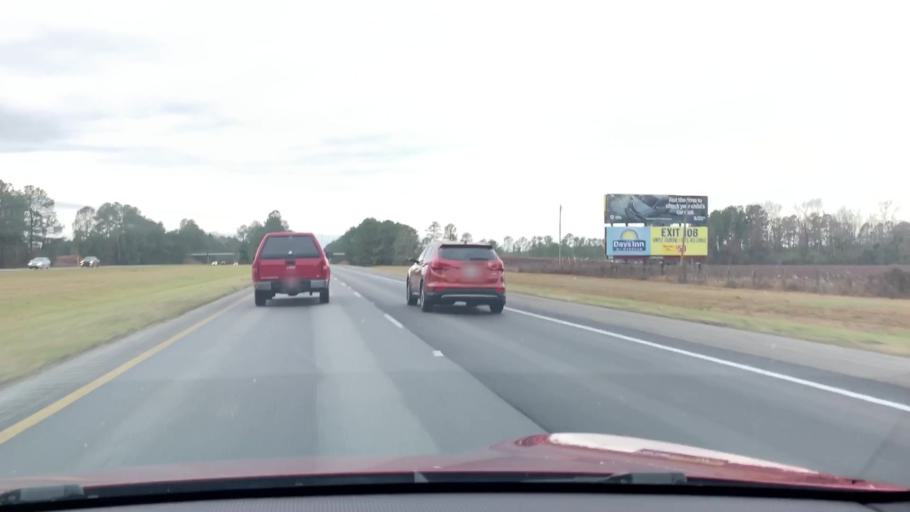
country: US
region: South Carolina
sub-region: Clarendon County
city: Manning
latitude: 33.6372
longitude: -80.2853
